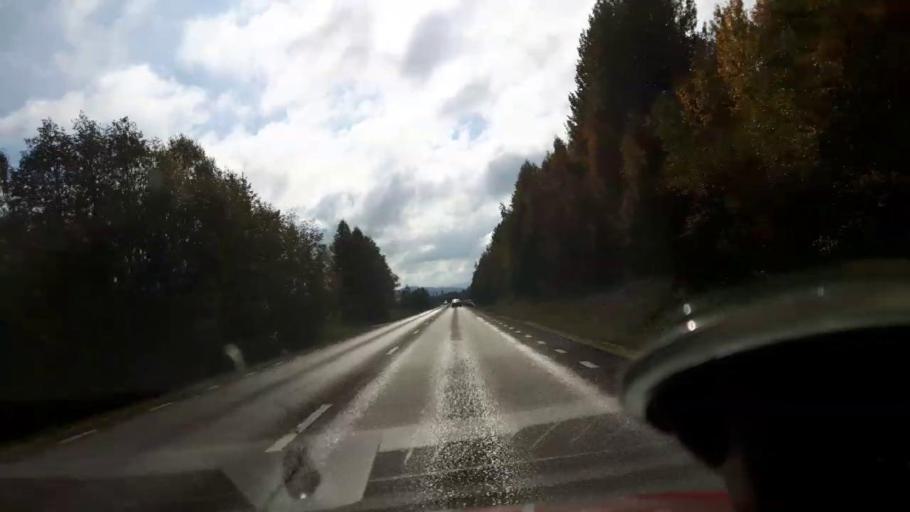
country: SE
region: Gaevleborg
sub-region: Ljusdals Kommun
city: Jaervsoe
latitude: 61.7327
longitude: 16.1641
